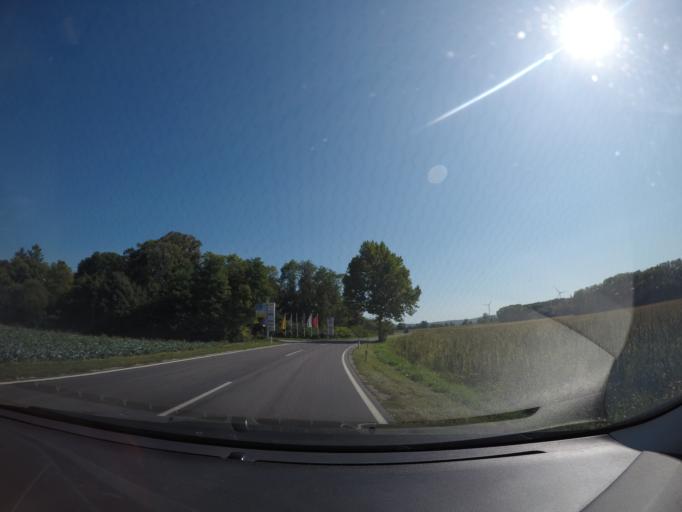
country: AT
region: Lower Austria
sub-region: Politischer Bezirk Baden
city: Seibersdorf
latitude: 47.9573
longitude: 16.5344
